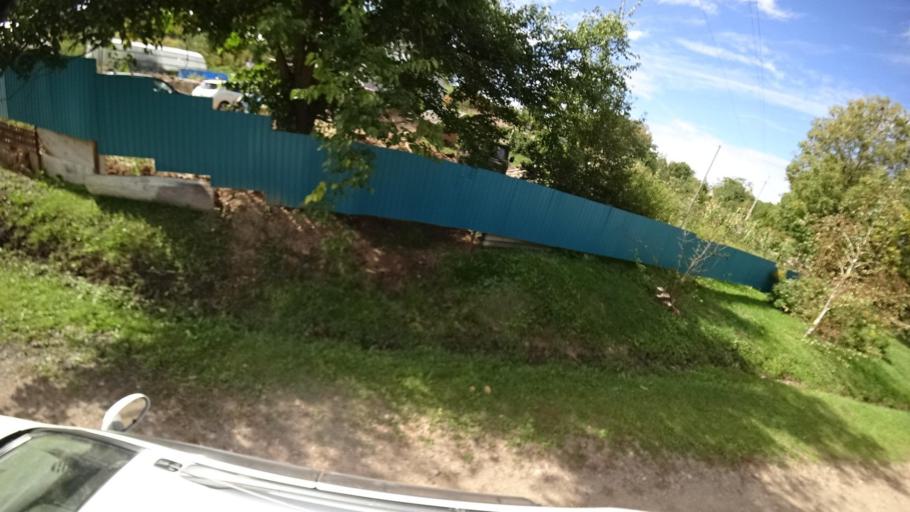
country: RU
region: Primorskiy
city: Yakovlevka
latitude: 44.3933
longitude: 133.6055
